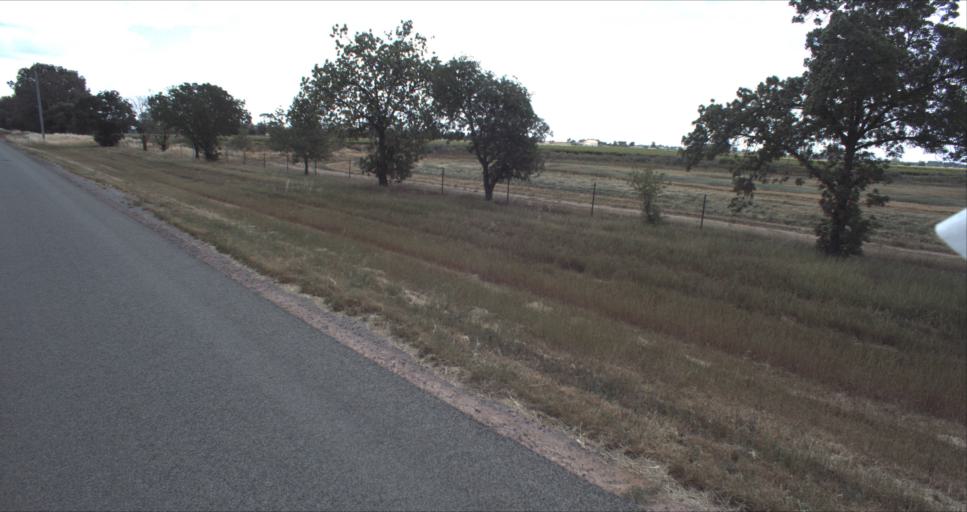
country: AU
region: New South Wales
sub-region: Leeton
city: Leeton
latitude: -34.5905
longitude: 146.4012
